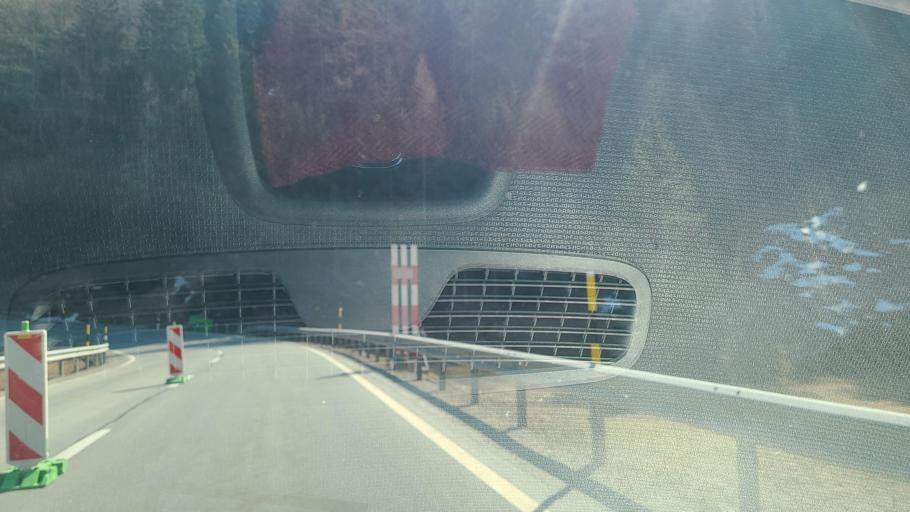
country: CH
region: Grisons
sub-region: Bernina District
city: Poschiavo
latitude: 46.3844
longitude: 10.0765
